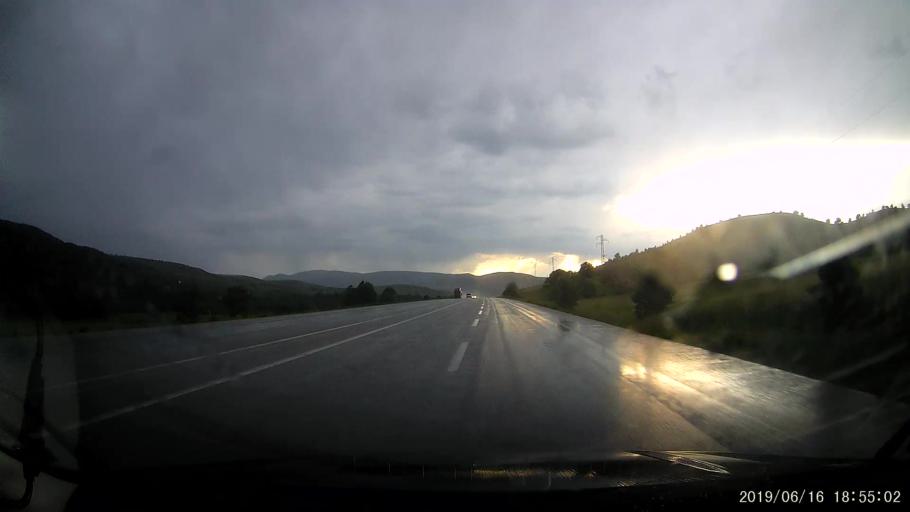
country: TR
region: Erzincan
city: Refahiye
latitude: 39.8986
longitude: 38.8381
